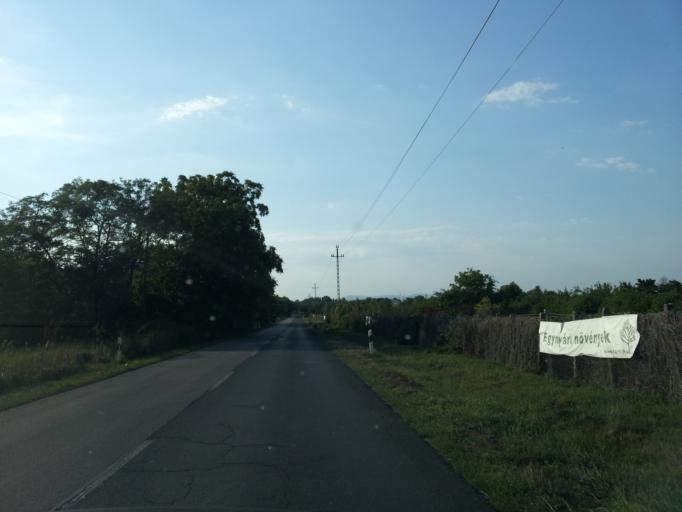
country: HU
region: Pest
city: Dunabogdany
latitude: 47.7656
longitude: 19.0649
